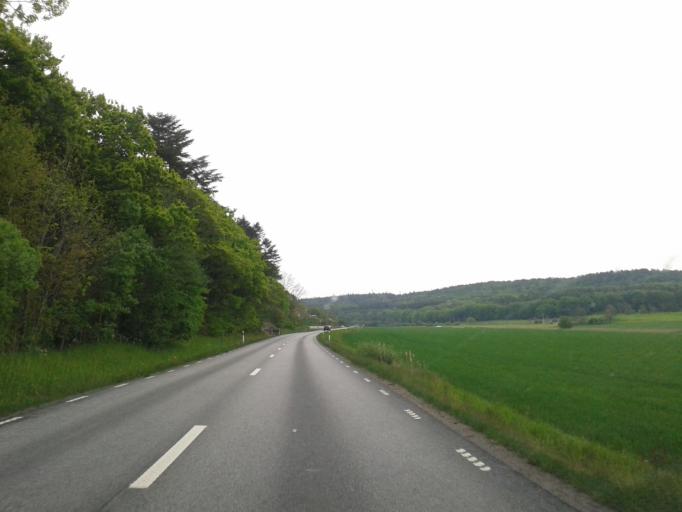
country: SE
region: Vaestra Goetaland
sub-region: Kungalvs Kommun
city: Kode
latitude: 57.8912
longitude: 11.7658
